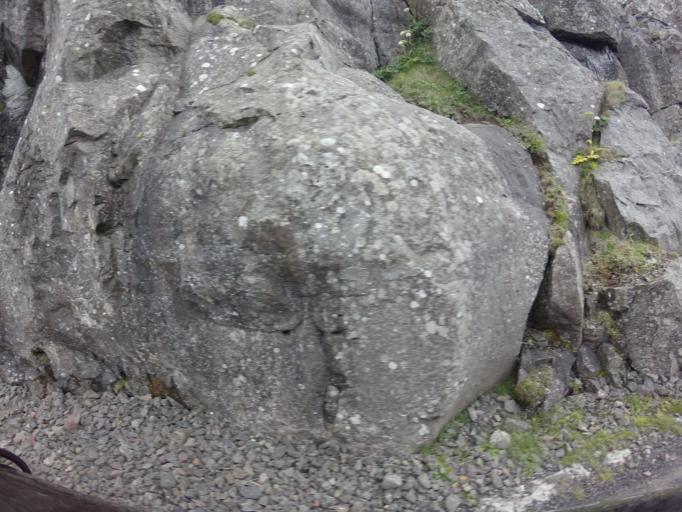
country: FO
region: Sandoy
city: Sandur
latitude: 61.8030
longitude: -6.7526
